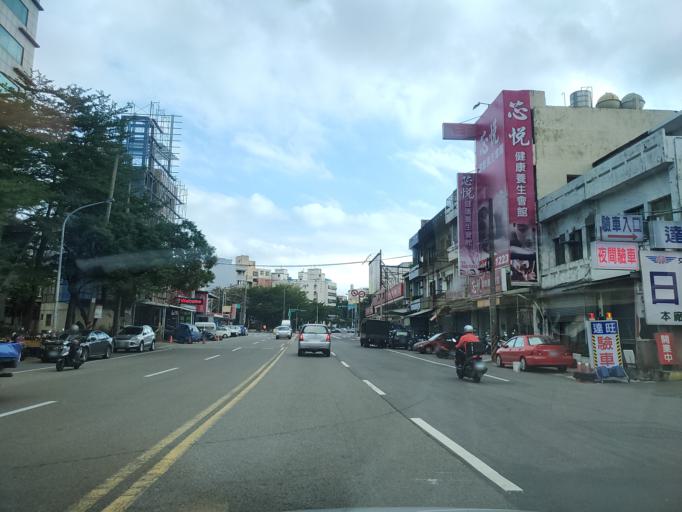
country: TW
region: Taiwan
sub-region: Hsinchu
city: Hsinchu
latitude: 24.8065
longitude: 120.9859
